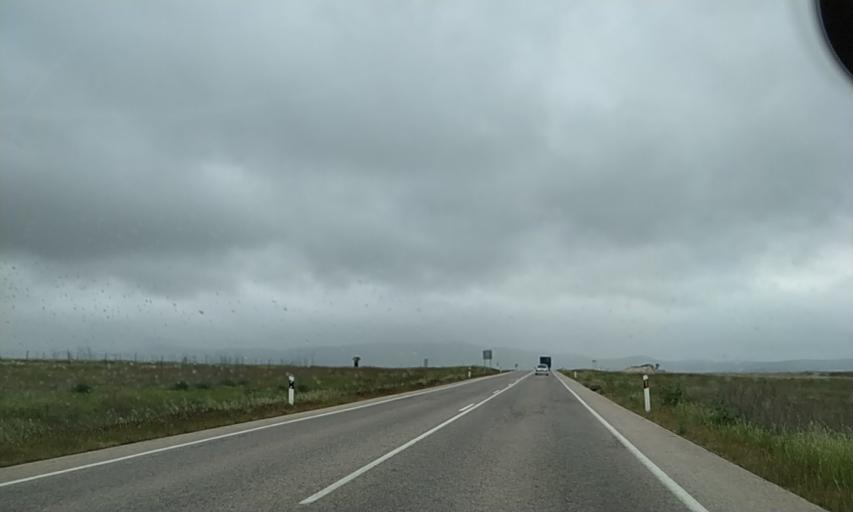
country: ES
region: Extremadura
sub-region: Provincia de Caceres
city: Malpartida de Caceres
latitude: 39.3491
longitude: -6.4705
